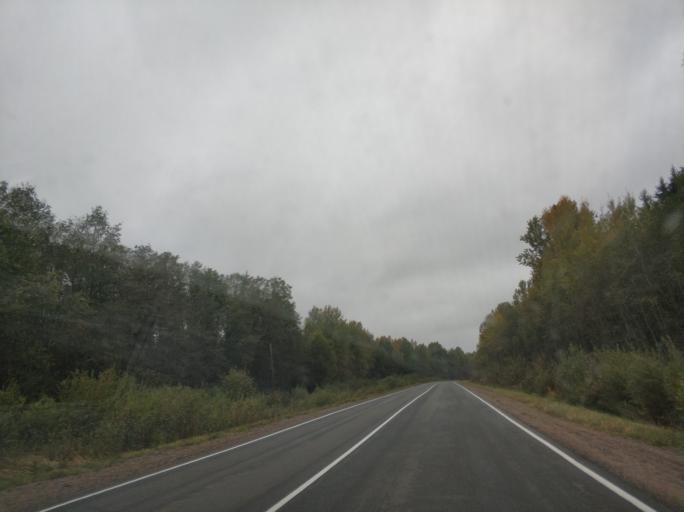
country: BY
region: Vitebsk
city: Rasony
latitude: 56.1066
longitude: 28.7191
